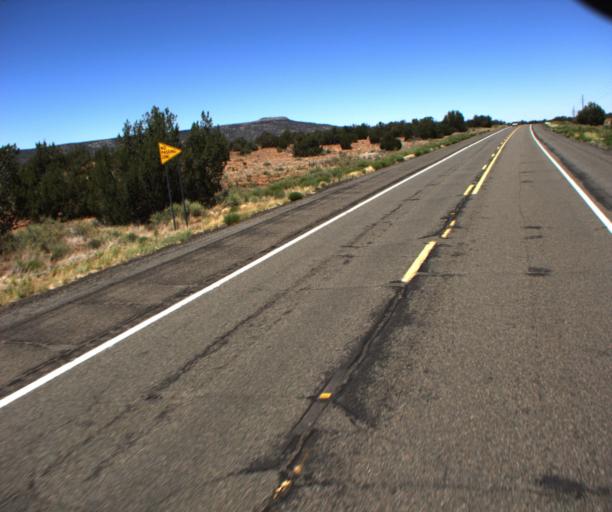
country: US
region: Arizona
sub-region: Coconino County
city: LeChee
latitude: 34.8249
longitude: -110.9577
